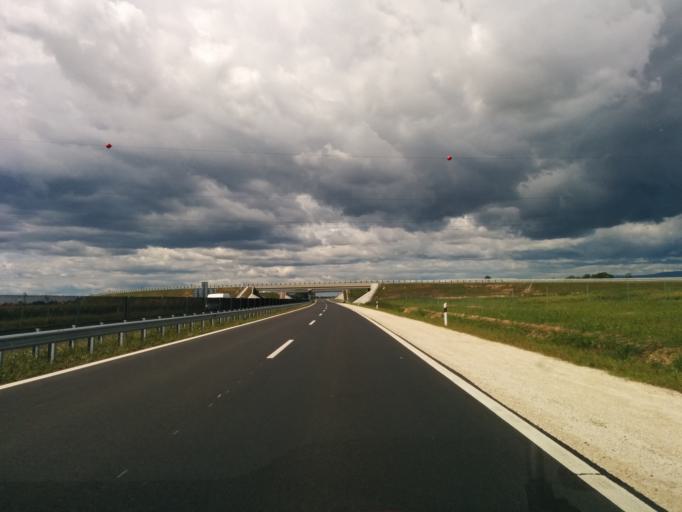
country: HU
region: Vas
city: Vep
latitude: 47.2553
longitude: 16.6999
